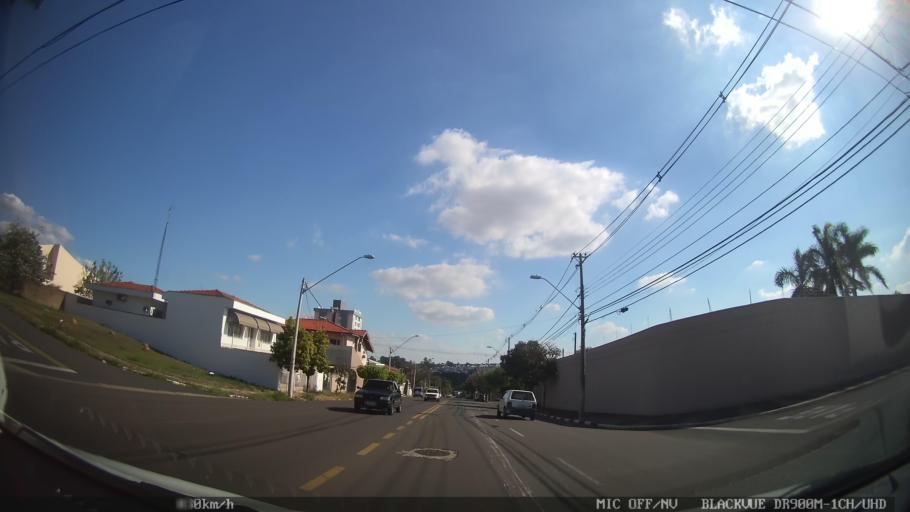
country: BR
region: Sao Paulo
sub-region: Sumare
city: Sumare
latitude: -22.8228
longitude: -47.2772
